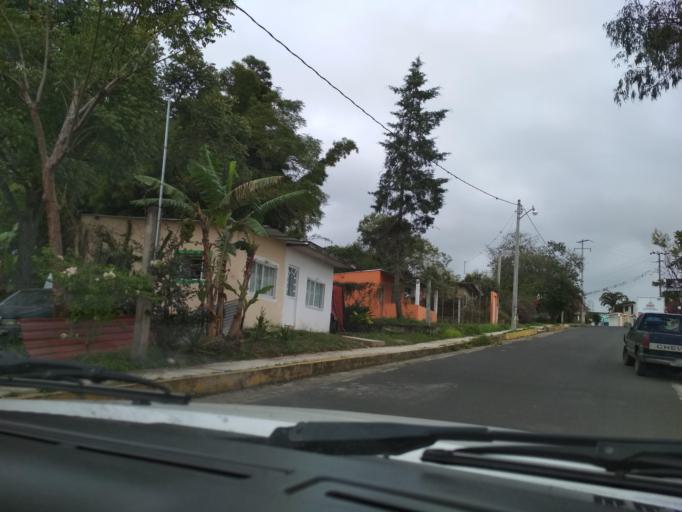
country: MX
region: Veracruz
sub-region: Emiliano Zapata
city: Dos Rios
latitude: 19.5212
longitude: -96.7957
